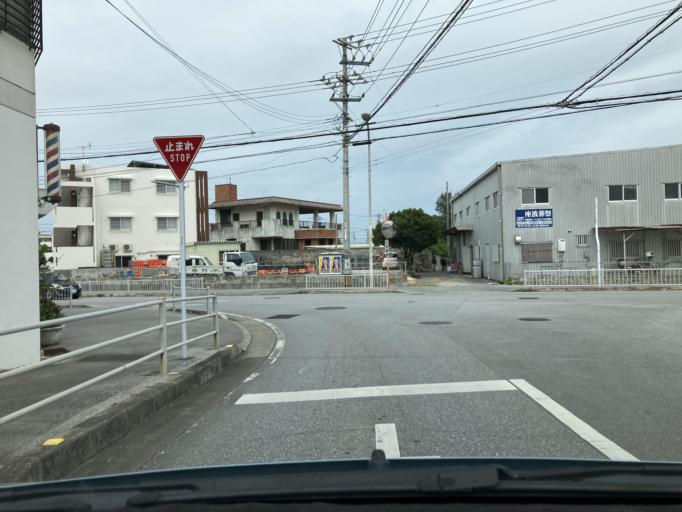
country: JP
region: Okinawa
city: Itoman
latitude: 26.1432
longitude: 127.6888
